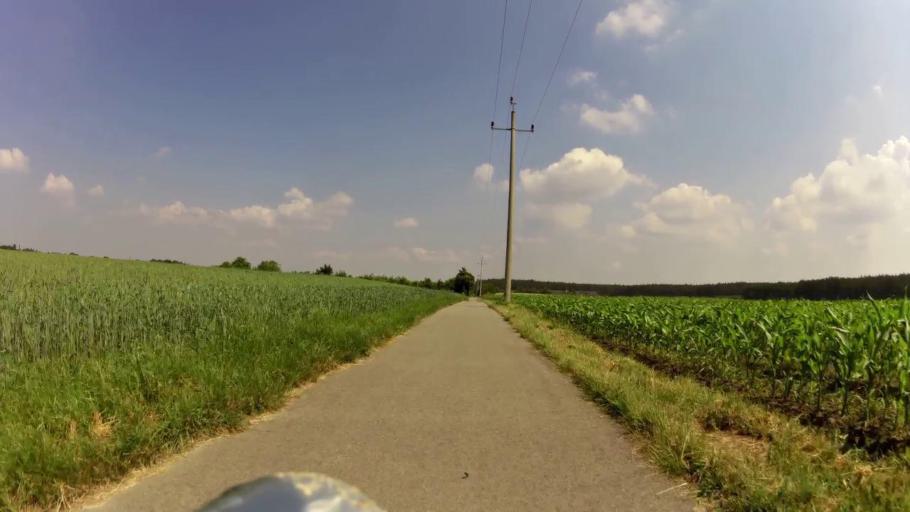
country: PL
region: Kujawsko-Pomorskie
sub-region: Powiat bydgoski
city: Koronowo
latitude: 53.2764
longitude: 17.9311
